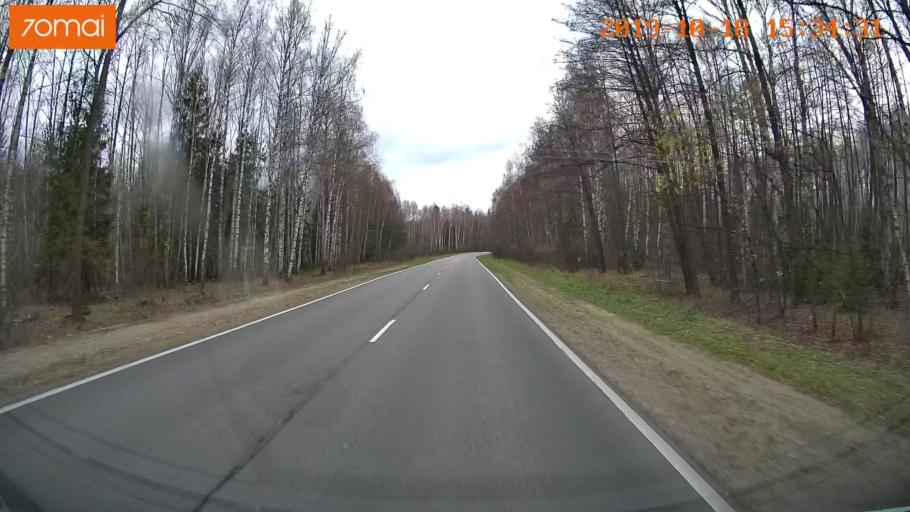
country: RU
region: Vladimir
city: Anopino
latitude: 55.8552
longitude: 40.6413
